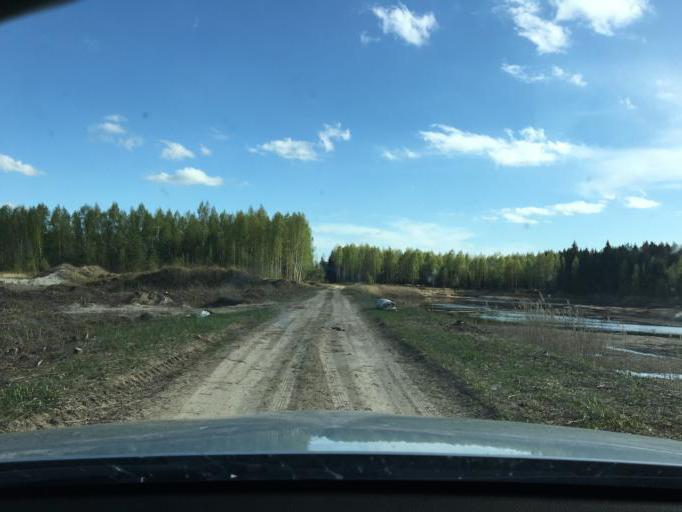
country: LV
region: Ozolnieku
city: Ozolnieki
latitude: 56.6644
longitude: 23.8659
